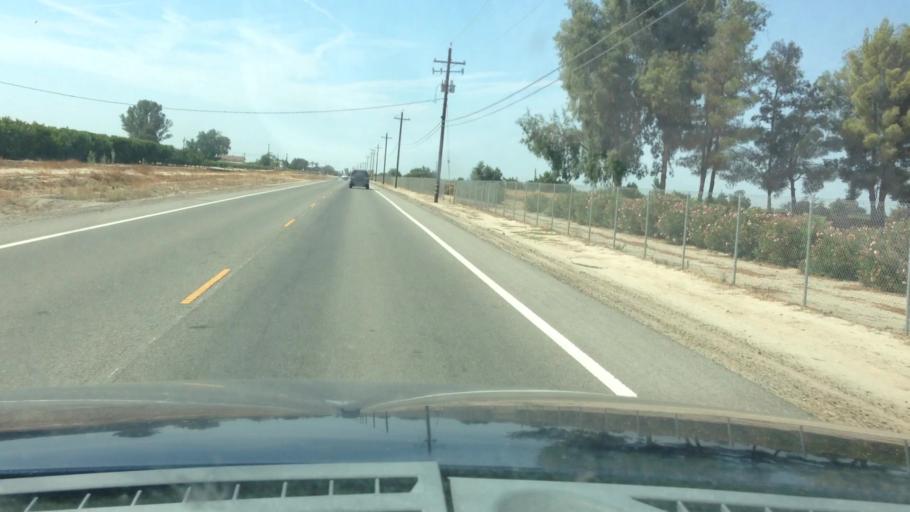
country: US
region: California
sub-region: Fresno County
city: Parlier
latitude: 36.5949
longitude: -119.5570
